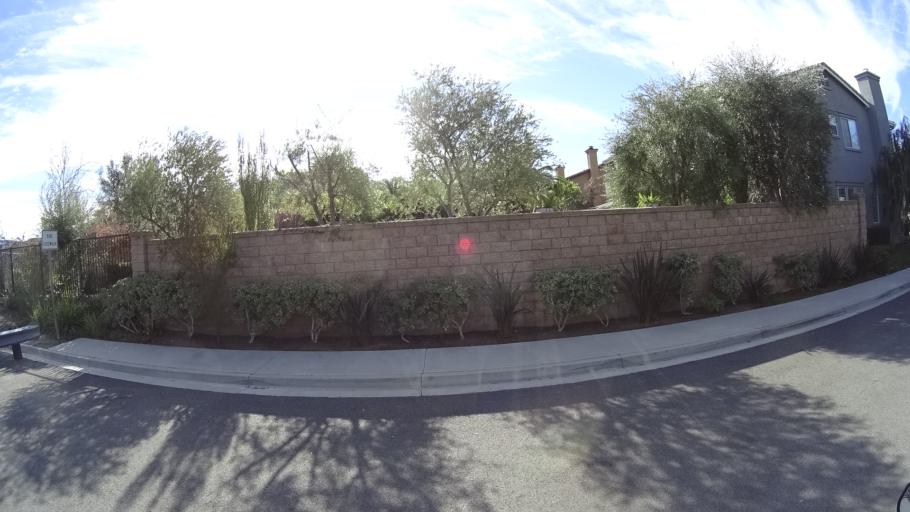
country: US
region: California
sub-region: Orange County
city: Portola Hills
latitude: 33.6909
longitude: -117.6186
